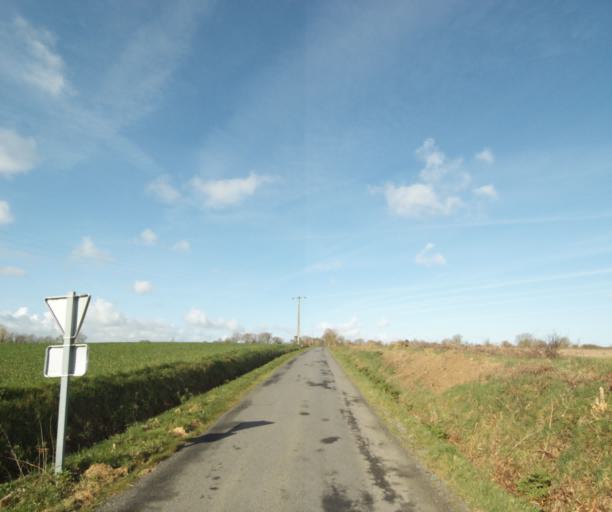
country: FR
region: Pays de la Loire
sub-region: Departement de la Loire-Atlantique
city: Bouvron
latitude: 47.4095
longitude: -1.8484
